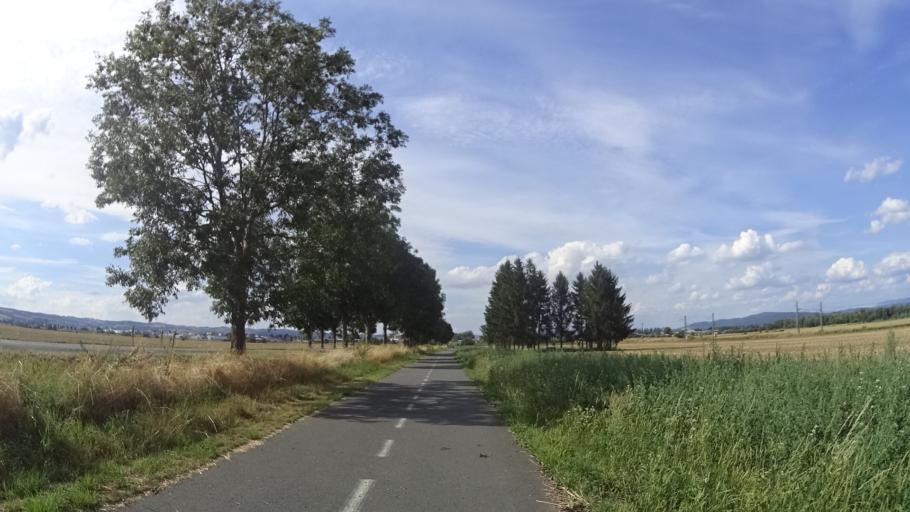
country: CZ
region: Olomoucky
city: Moravicany
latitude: 49.7632
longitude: 16.9506
